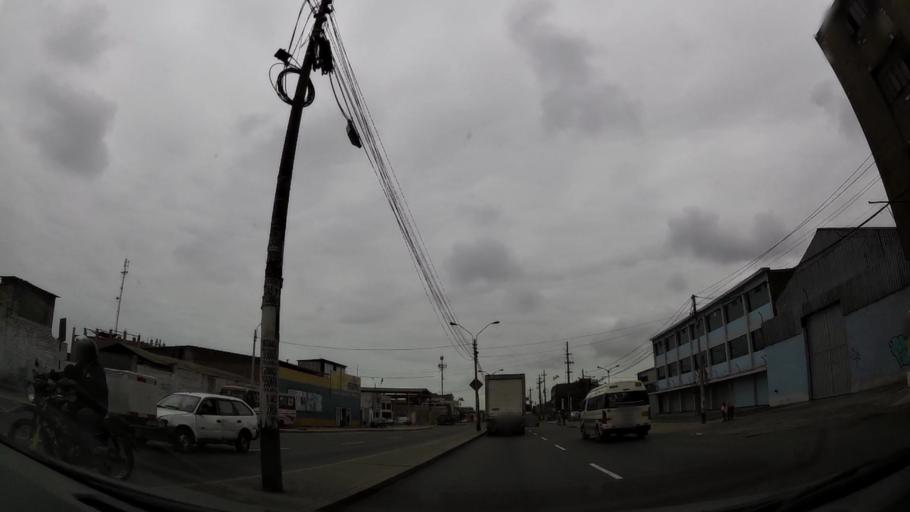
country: PE
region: Callao
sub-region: Callao
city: Callao
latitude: -12.0465
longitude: -77.0773
